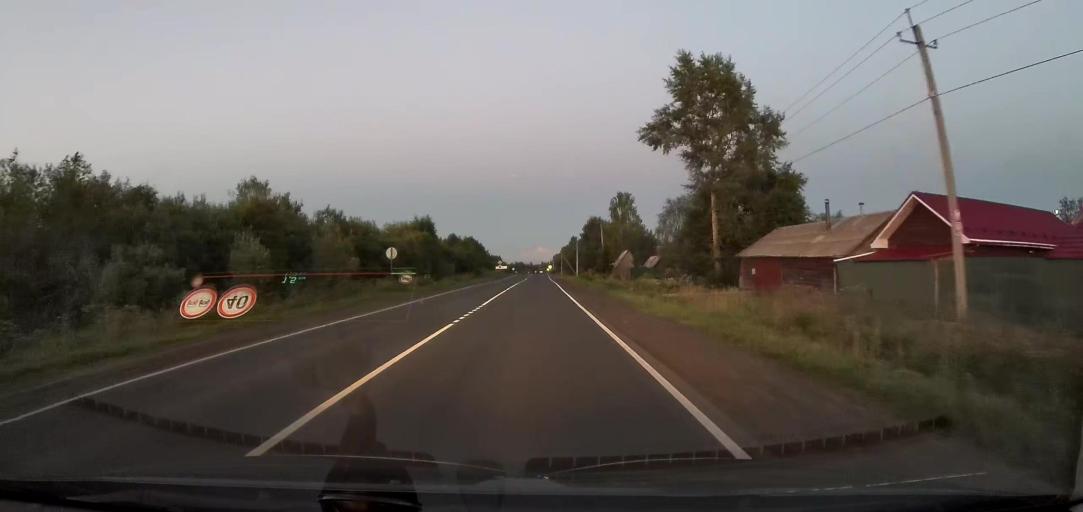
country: RU
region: Arkhangelskaya
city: Uyemskiy
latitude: 64.4458
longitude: 40.9488
